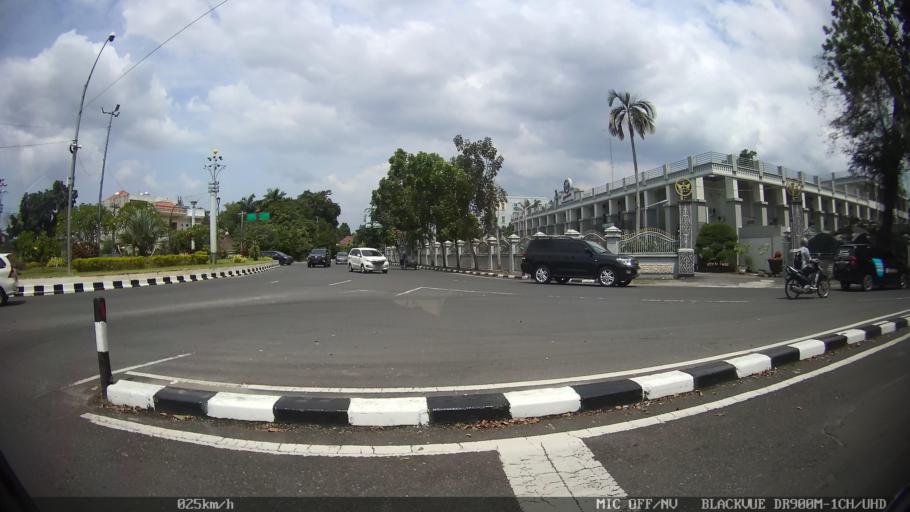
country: ID
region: North Sumatra
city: Medan
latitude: 3.5719
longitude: 98.6720
